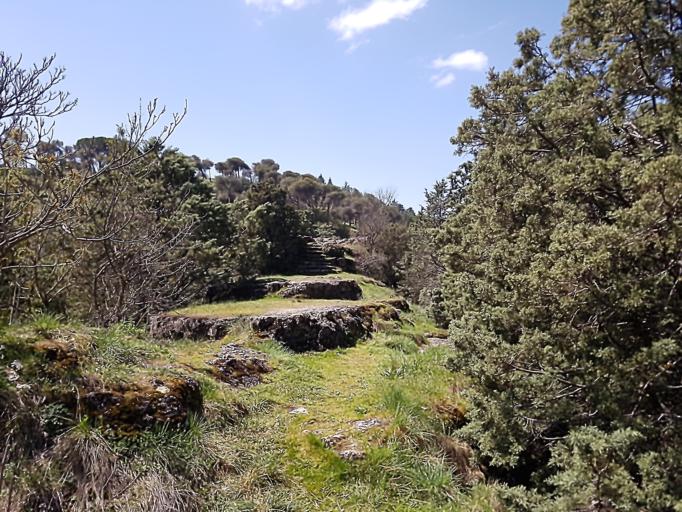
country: ES
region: Castille and Leon
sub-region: Provincia de Segovia
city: Segovia
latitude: 40.9511
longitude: -4.1301
